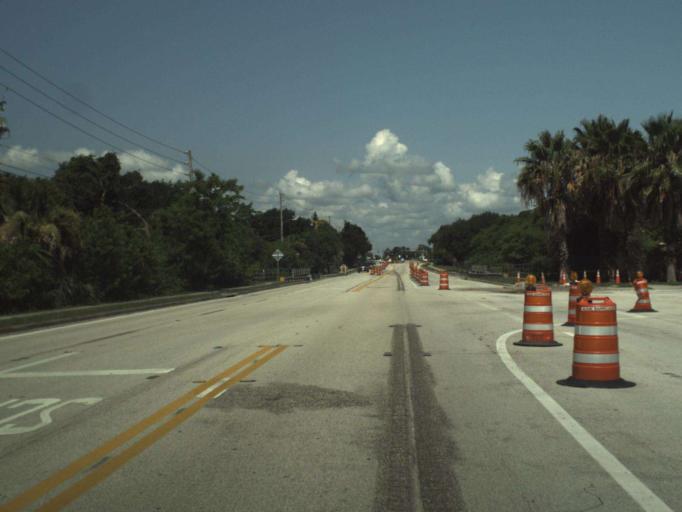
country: US
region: Florida
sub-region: Brevard County
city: West Melbourne
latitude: 28.1288
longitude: -80.6489
